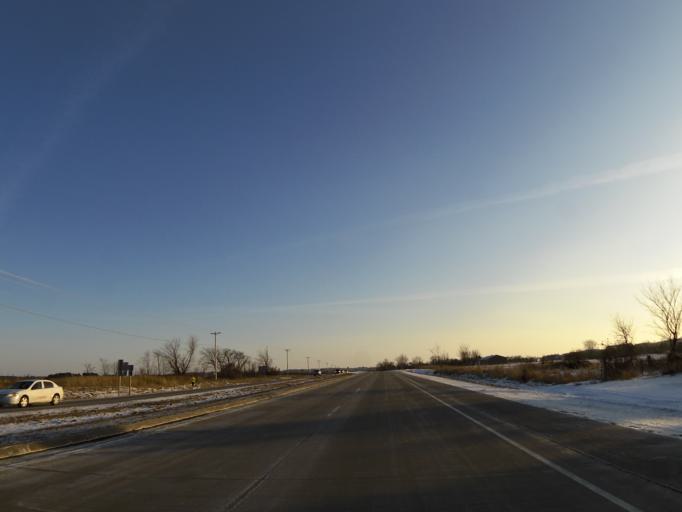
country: US
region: Wisconsin
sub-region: Saint Croix County
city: North Hudson
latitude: 44.9856
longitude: -92.6803
